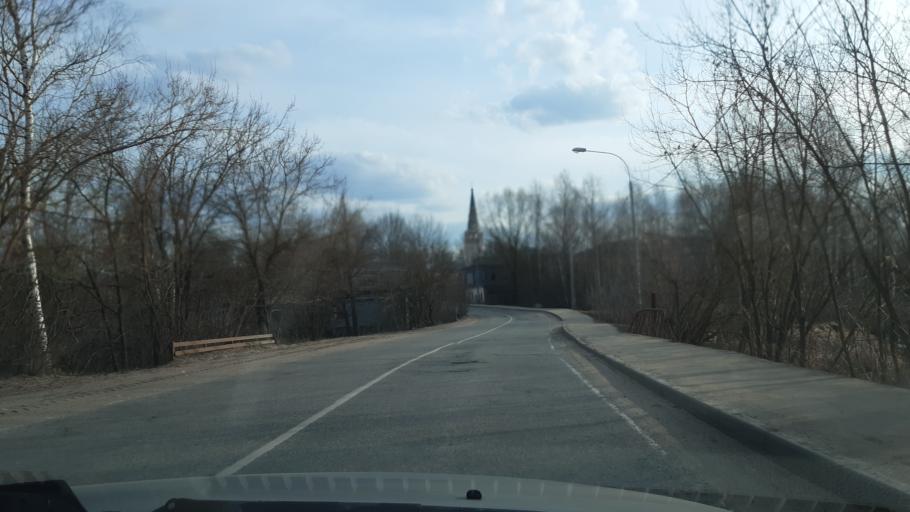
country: RU
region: Vladimir
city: Nikologory
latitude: 56.1433
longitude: 41.9937
